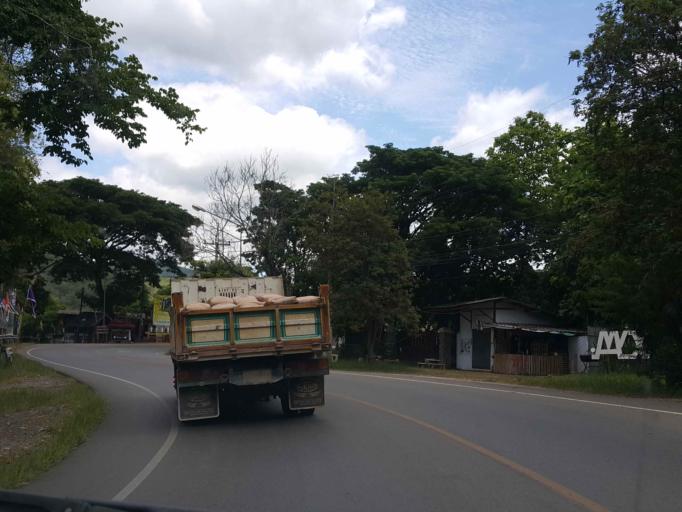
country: TH
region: Chiang Mai
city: Hang Dong
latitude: 18.7510
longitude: 98.8894
